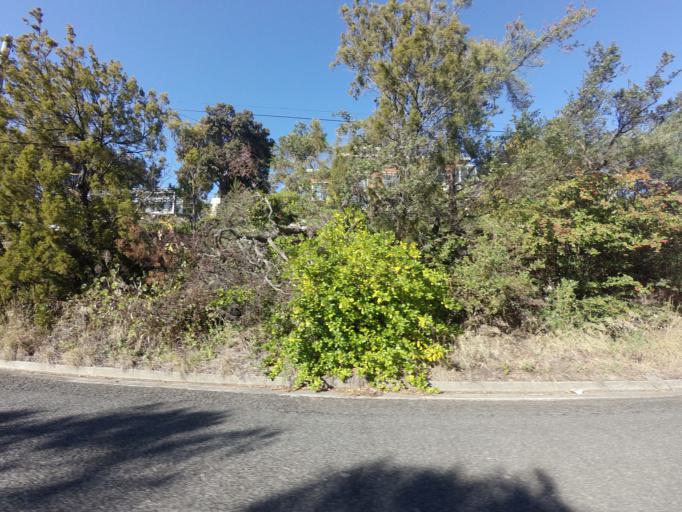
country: AU
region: Tasmania
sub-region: Clarence
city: Lindisfarne
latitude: -42.8435
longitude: 147.3390
